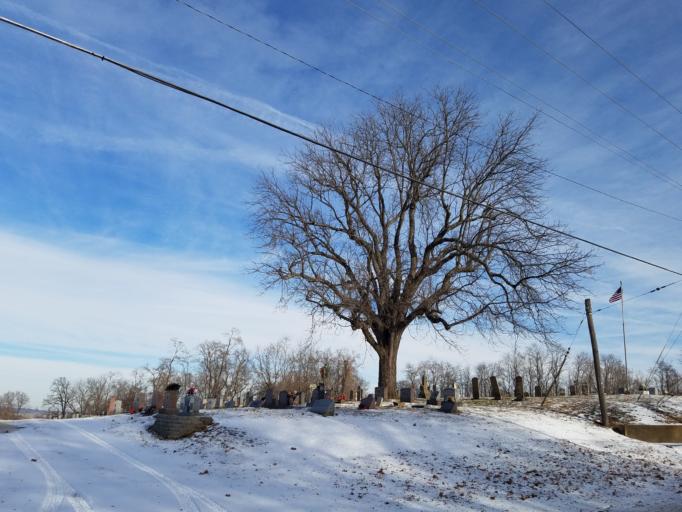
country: US
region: Missouri
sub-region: Lafayette County
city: Lexington
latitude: 39.1321
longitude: -93.9911
